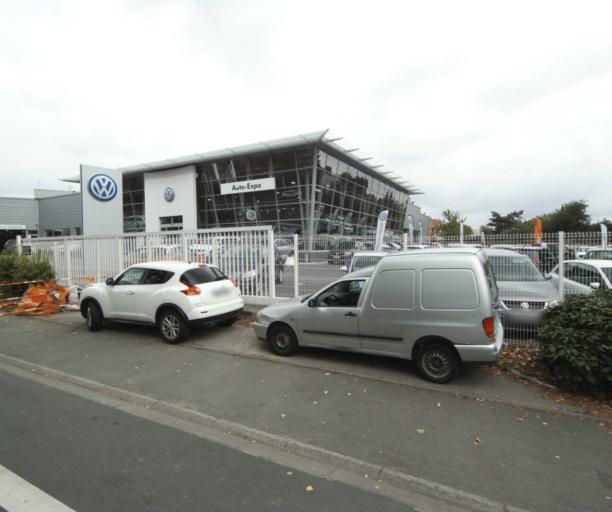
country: FR
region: Nord-Pas-de-Calais
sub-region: Departement du Nord
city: Mons-en-Baroeul
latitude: 50.6380
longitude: 3.1325
